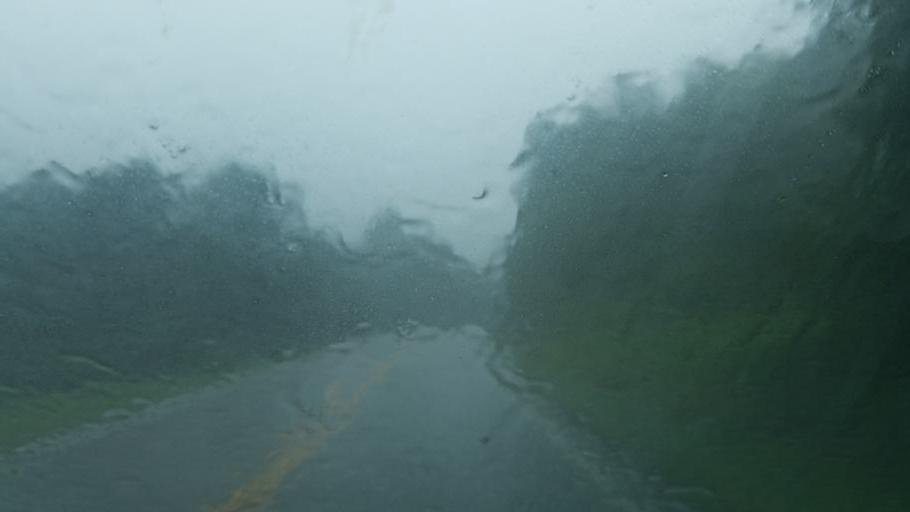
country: US
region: Kentucky
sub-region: Rowan County
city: Morehead
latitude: 38.2711
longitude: -83.5392
